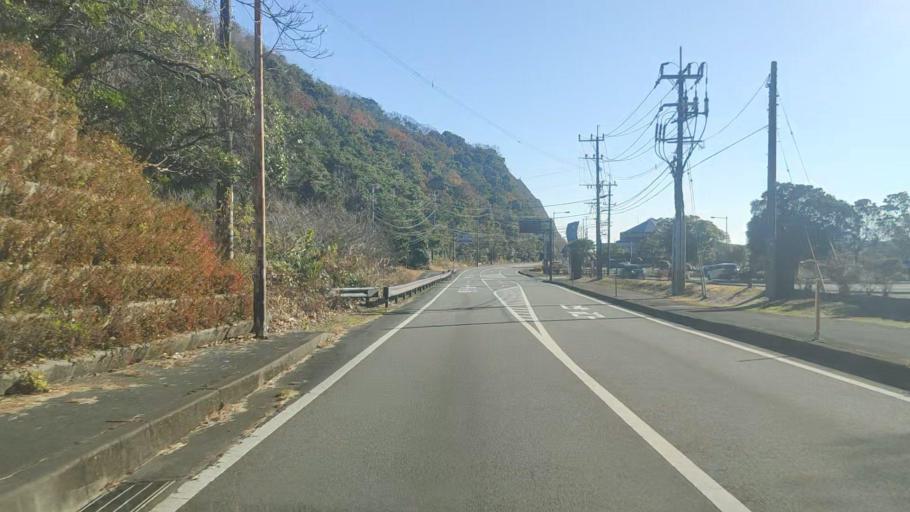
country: JP
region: Miyazaki
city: Nobeoka
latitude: 32.6857
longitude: 131.7987
